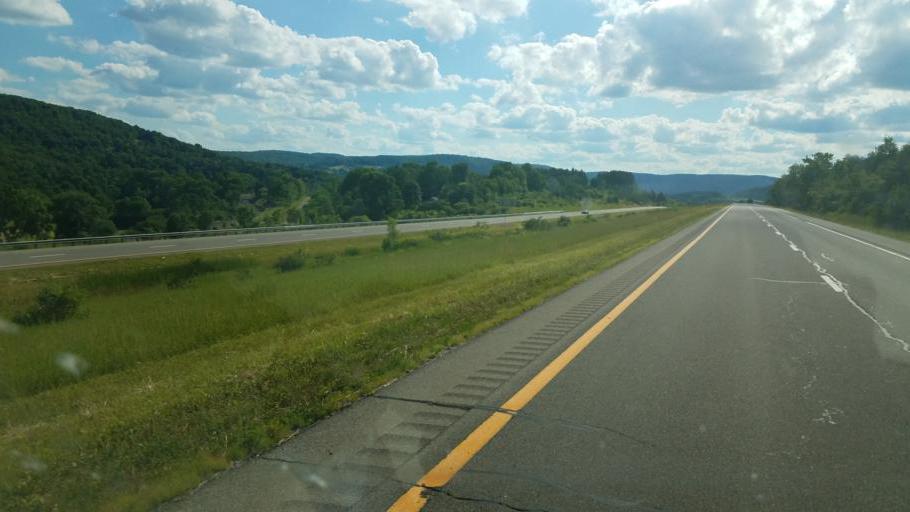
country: US
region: New York
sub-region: Allegany County
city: Cuba
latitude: 42.2265
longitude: -78.2548
